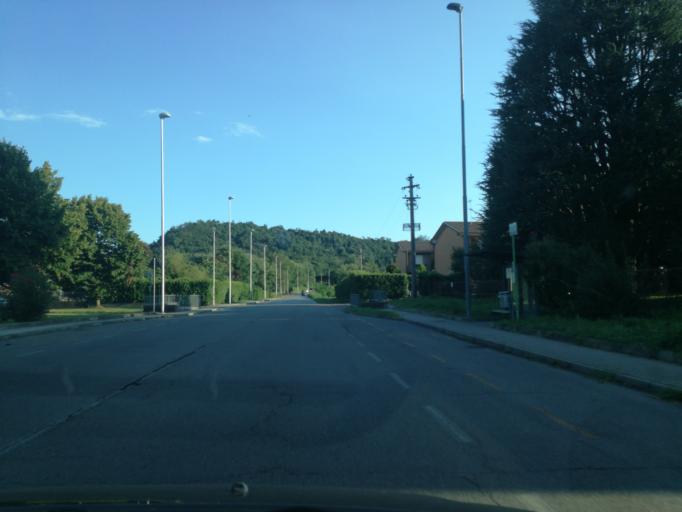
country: IT
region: Lombardy
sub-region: Provincia di Lecco
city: Imbersago
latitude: 45.7057
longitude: 9.4493
